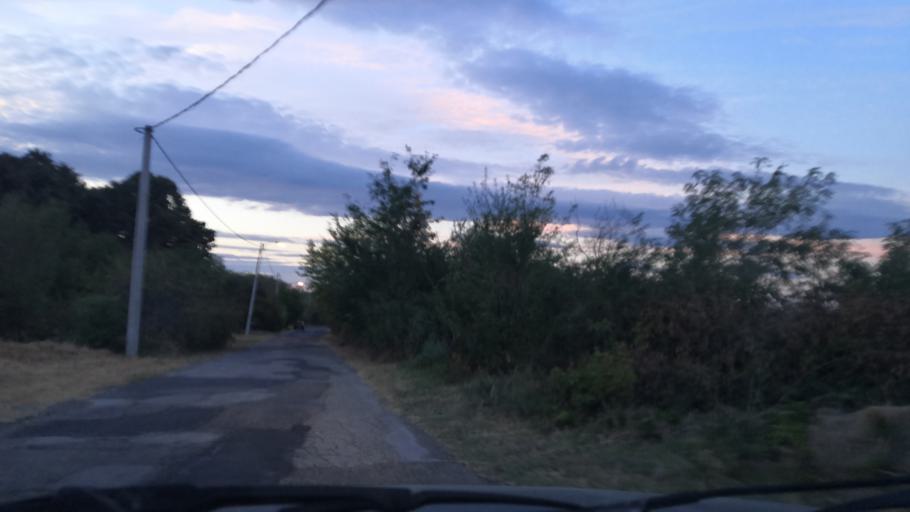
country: RO
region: Mehedinti
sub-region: Comuna Gogosu
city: Balta Verde
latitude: 44.3093
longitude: 22.5489
